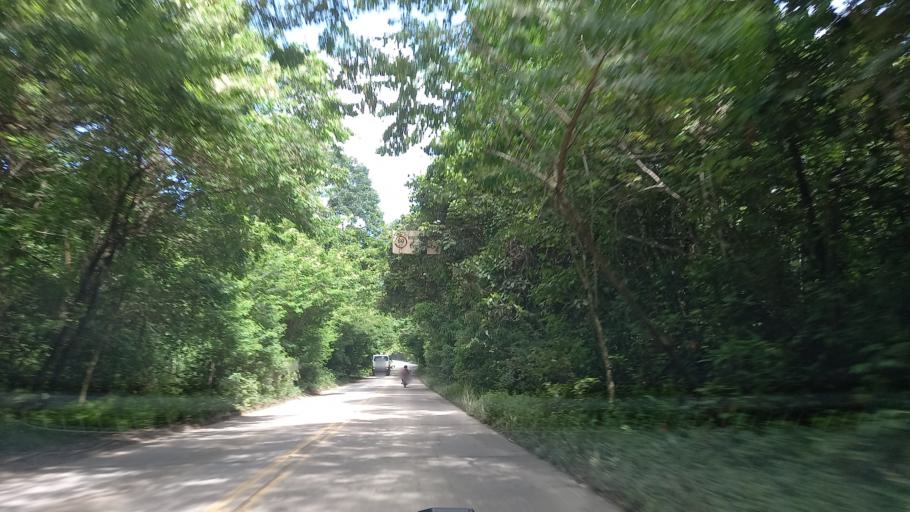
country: BR
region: Pernambuco
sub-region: Rio Formoso
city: Rio Formoso
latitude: -8.7302
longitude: -35.1733
